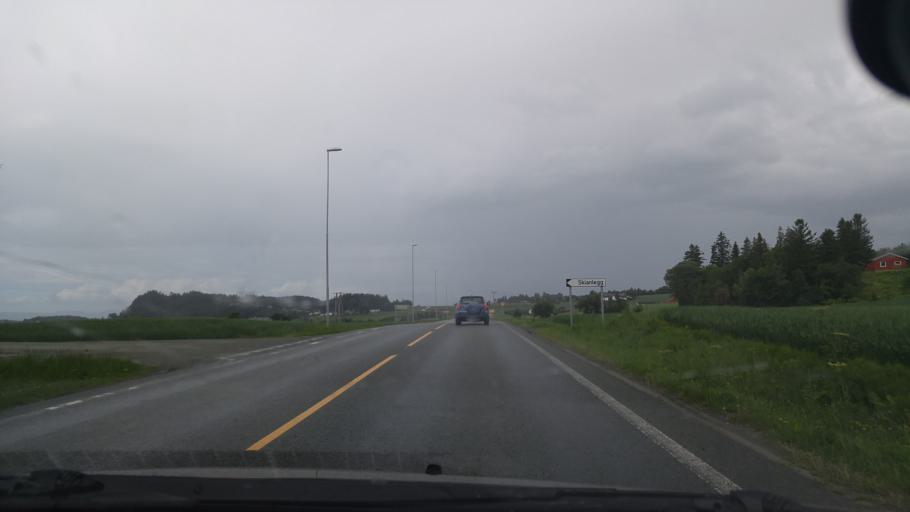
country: NO
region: Nord-Trondelag
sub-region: Stjordal
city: Stjordal
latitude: 63.5212
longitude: 10.8518
